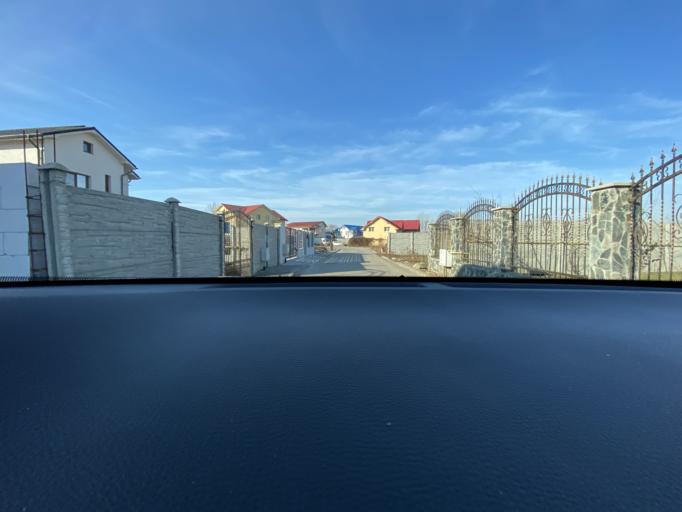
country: RO
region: Olt
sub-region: Municipiul Slatina
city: Slatina
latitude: 44.4376
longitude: 24.3745
